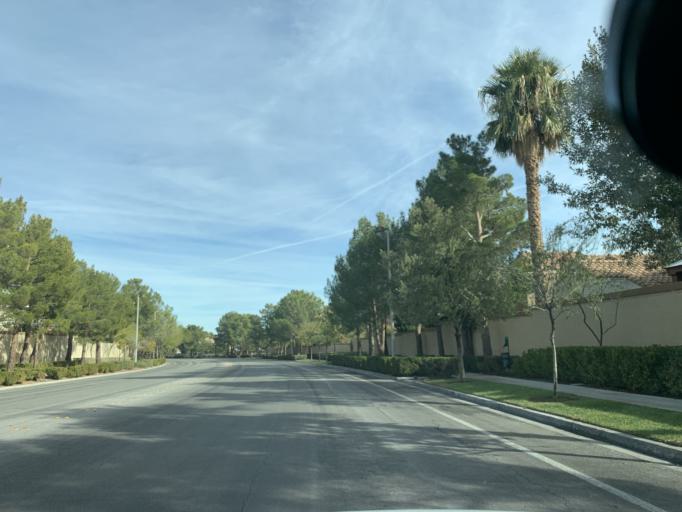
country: US
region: Nevada
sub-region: Clark County
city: Summerlin South
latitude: 36.1505
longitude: -115.3000
